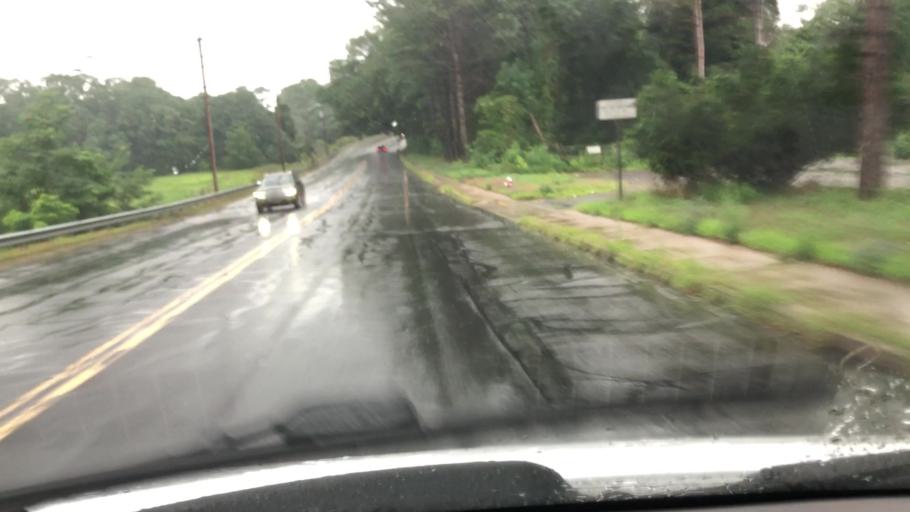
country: US
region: Massachusetts
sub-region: Hampshire County
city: Northampton
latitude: 42.3333
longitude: -72.6590
